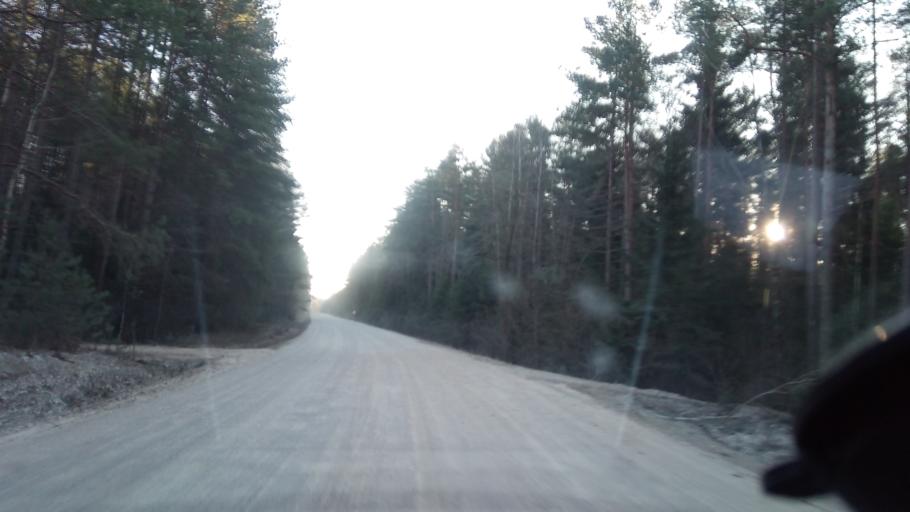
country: LT
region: Alytaus apskritis
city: Druskininkai
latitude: 54.1468
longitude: 23.9390
